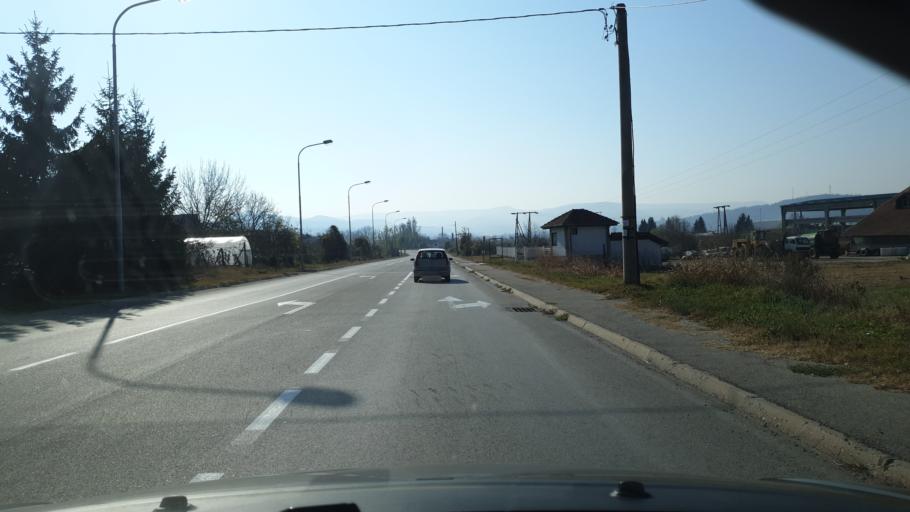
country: RS
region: Central Serbia
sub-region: Zajecarski Okrug
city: Knjazevac
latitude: 43.5872
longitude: 22.2687
